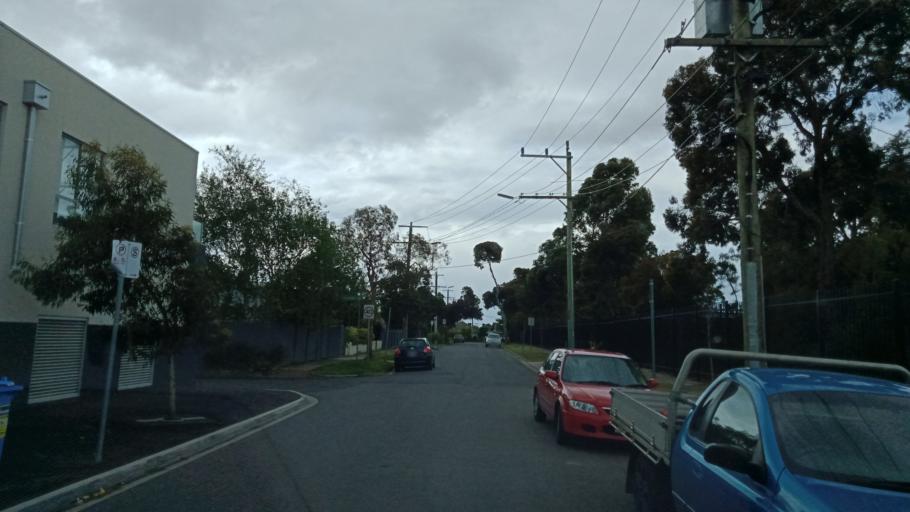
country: AU
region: Victoria
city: McKinnon
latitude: -37.9279
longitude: 145.0593
